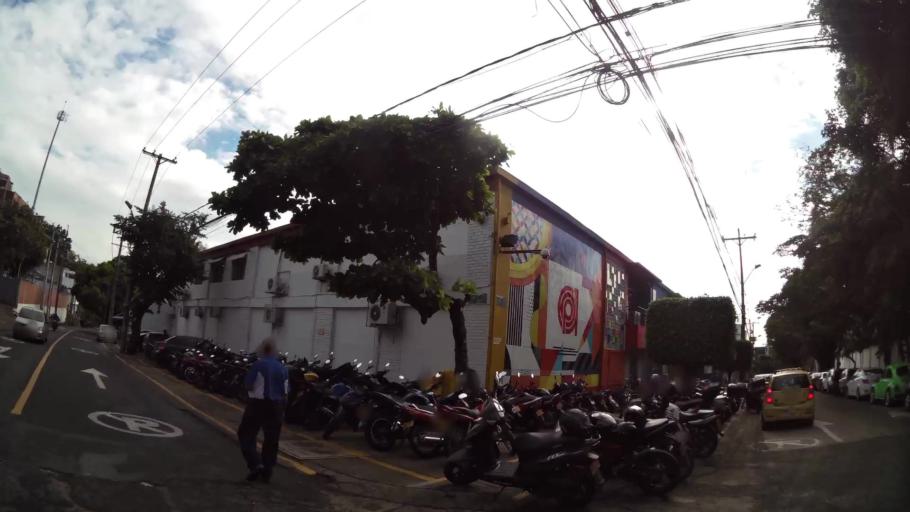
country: CO
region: Valle del Cauca
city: Cali
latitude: 3.4703
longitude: -76.5313
